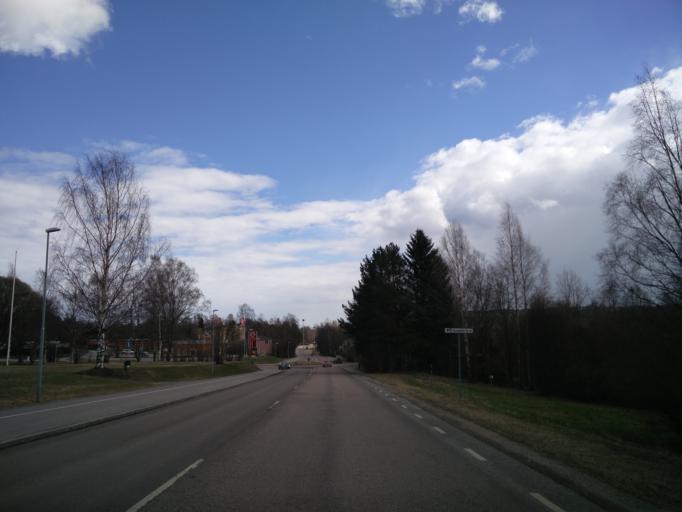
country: SE
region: Vaesternorrland
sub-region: Sundsvalls Kommun
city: Sundsvall
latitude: 62.4003
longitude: 17.2580
